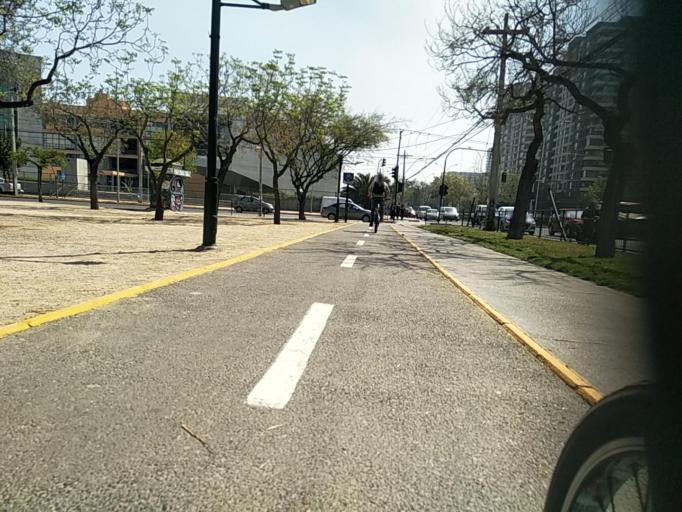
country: CL
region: Santiago Metropolitan
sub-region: Provincia de Santiago
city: Villa Presidente Frei, Nunoa, Santiago, Chile
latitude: -33.4650
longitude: -70.5937
